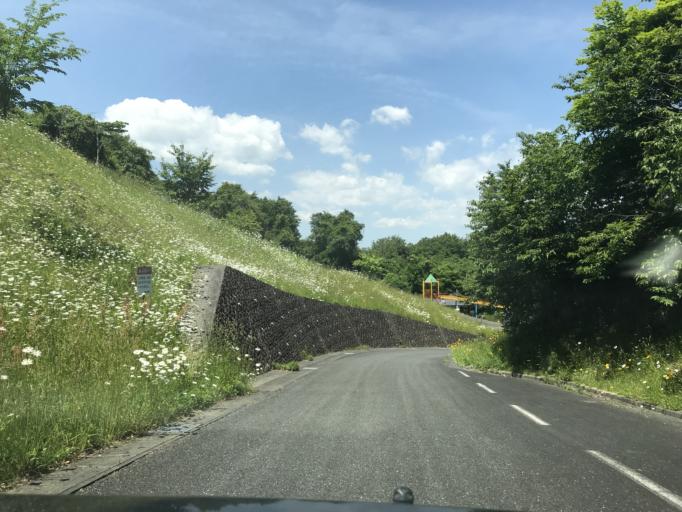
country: JP
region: Iwate
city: Ichinoseki
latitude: 38.9165
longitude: 141.1223
